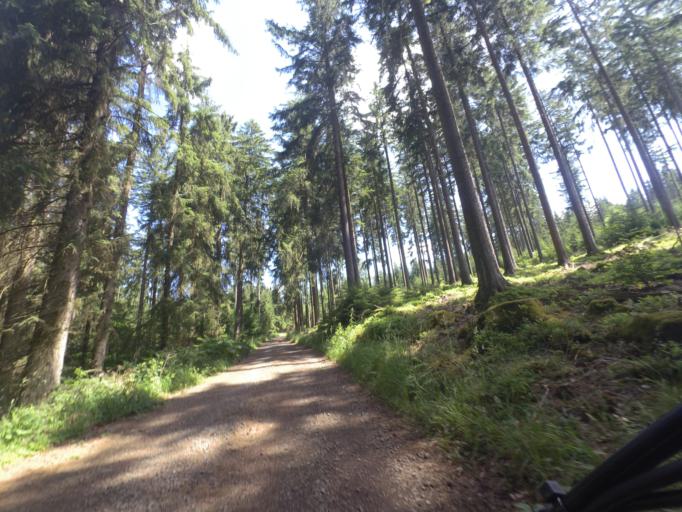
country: DE
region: Rheinland-Pfalz
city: Junkerath
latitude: 50.3144
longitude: 6.5571
